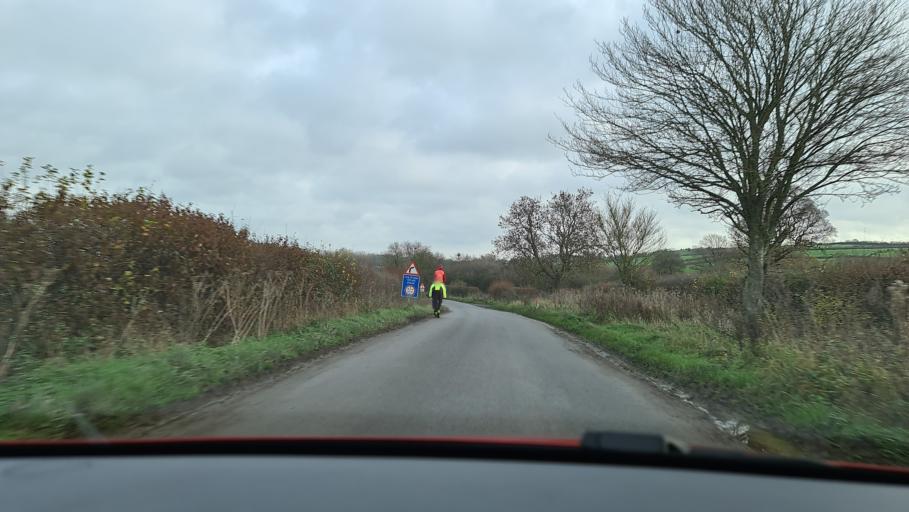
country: GB
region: England
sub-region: Buckinghamshire
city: Long Crendon
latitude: 51.7960
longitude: -0.9819
